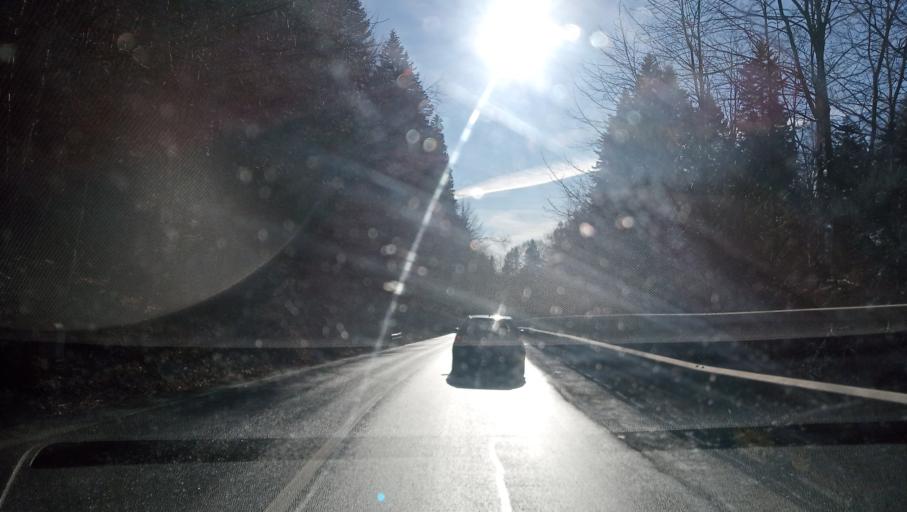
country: RO
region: Brasov
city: Crivina
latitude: 45.4711
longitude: 25.9295
